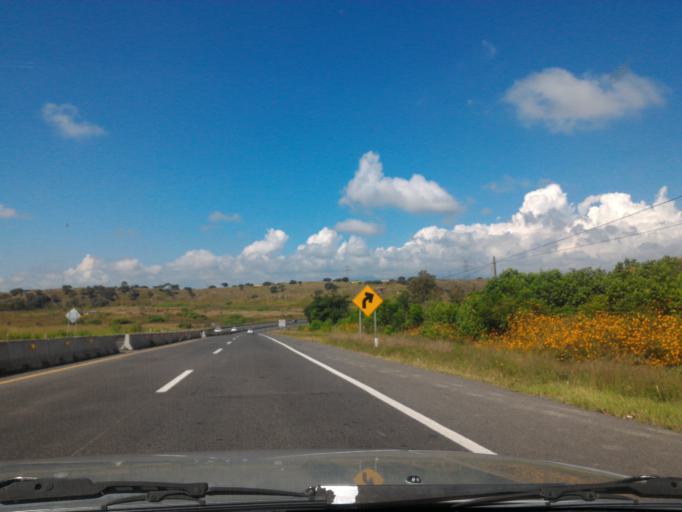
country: MX
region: Jalisco
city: La Venta del Astillero
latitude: 20.7319
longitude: -103.6175
